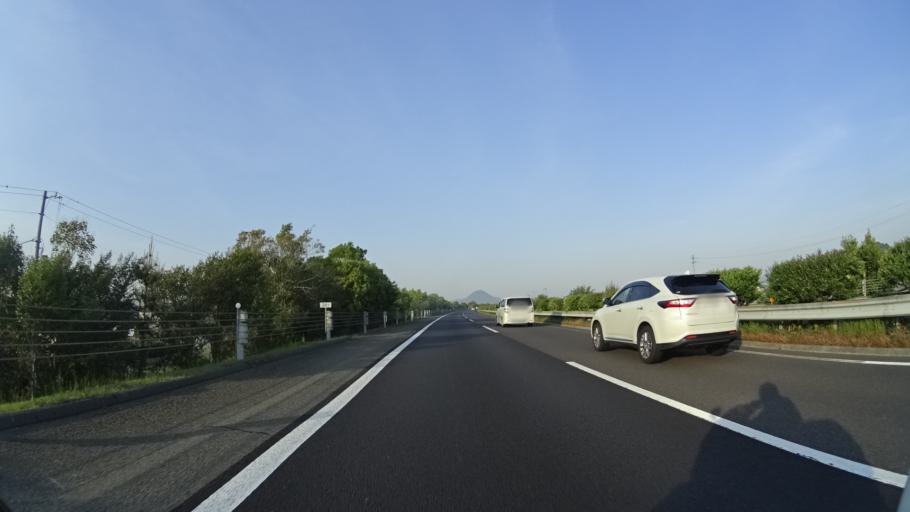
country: JP
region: Kagawa
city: Tadotsu
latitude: 34.2367
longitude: 133.7544
